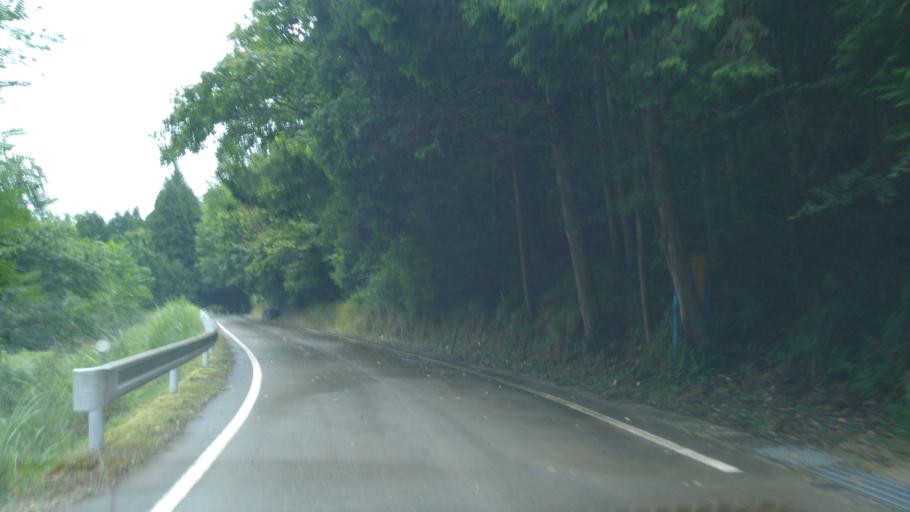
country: JP
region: Kyoto
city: Ayabe
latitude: 35.2378
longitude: 135.2658
